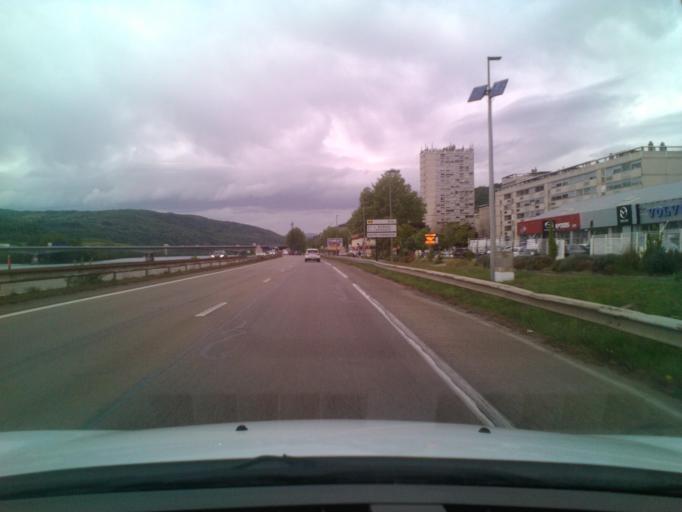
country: FR
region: Rhone-Alpes
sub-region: Departement du Rhone
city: Saint-Romain-en-Gal
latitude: 45.5391
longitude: 4.8631
